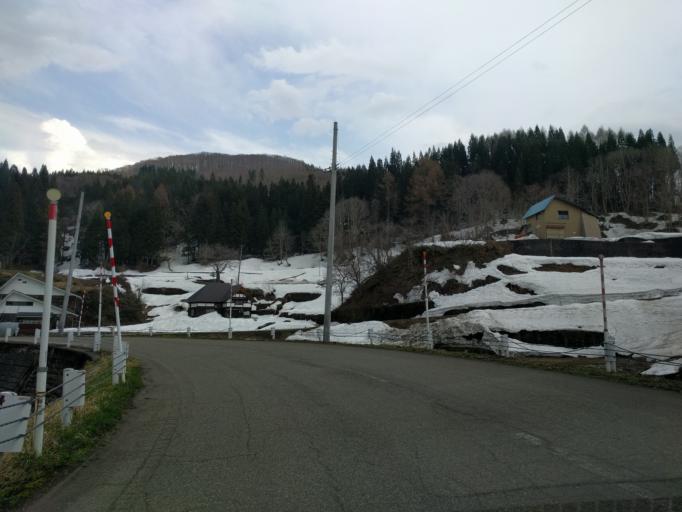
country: JP
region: Niigata
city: Muramatsu
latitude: 37.3392
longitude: 139.4956
